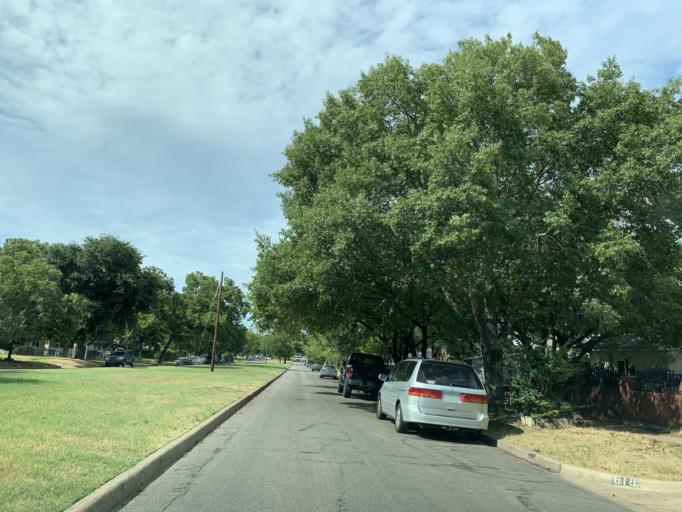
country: US
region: Texas
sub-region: Dallas County
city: Cockrell Hill
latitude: 32.7376
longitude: -96.8528
